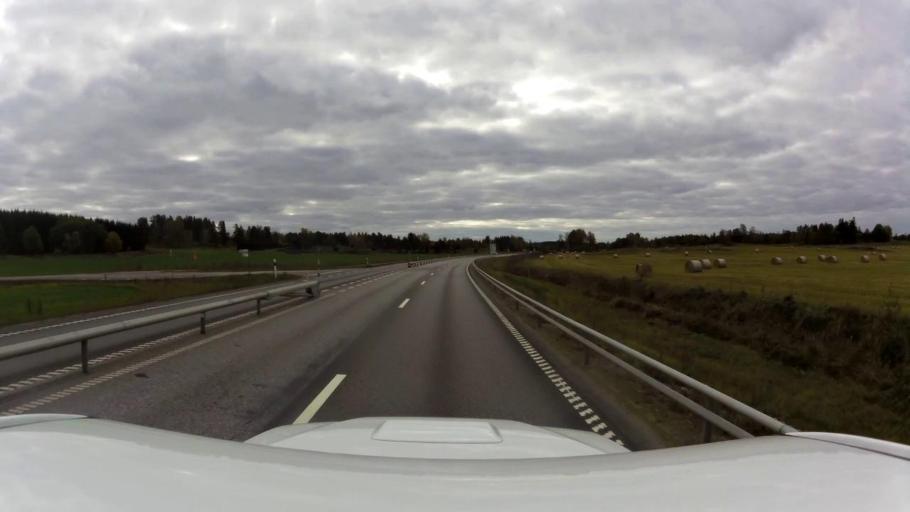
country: SE
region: OEstergoetland
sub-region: Linkopings Kommun
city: Malmslatt
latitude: 58.3226
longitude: 15.5672
